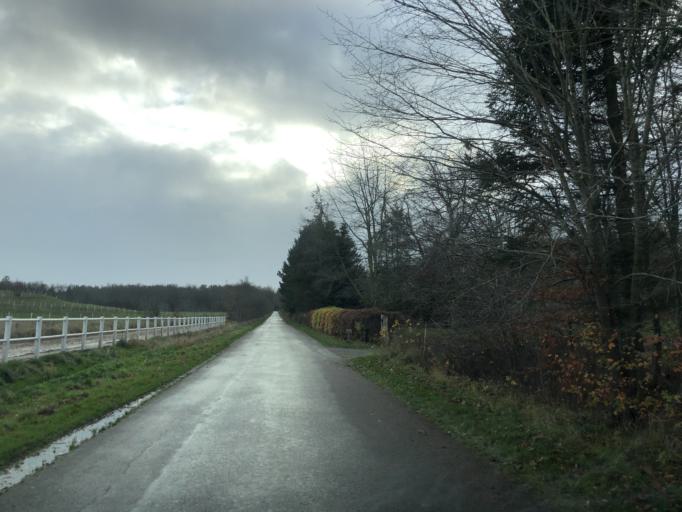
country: DK
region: North Denmark
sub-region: Rebild Kommune
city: Stovring
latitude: 56.9318
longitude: 9.8042
